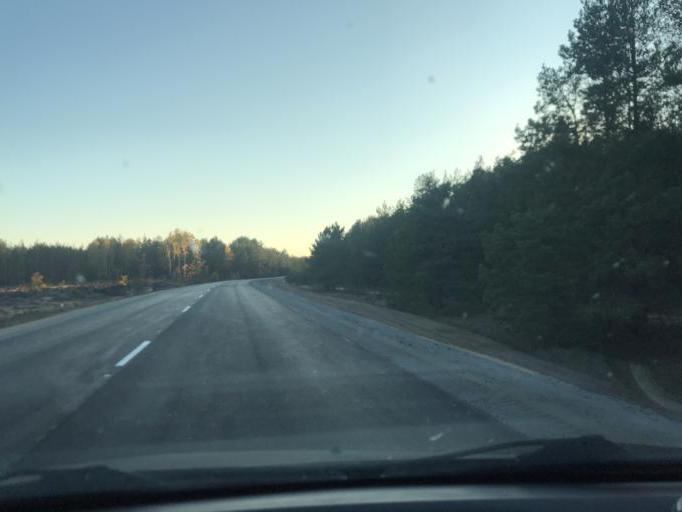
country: BY
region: Gomel
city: Brahin
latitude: 51.8610
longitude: 30.3700
